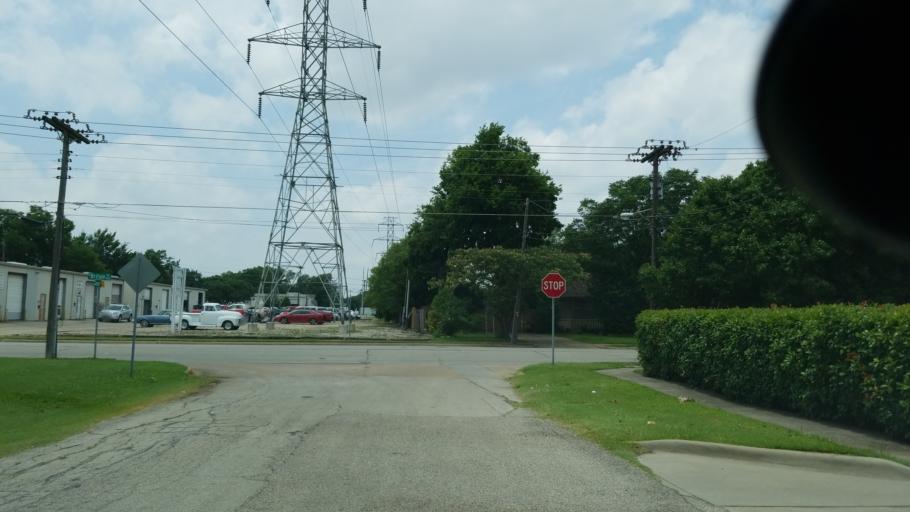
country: US
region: Texas
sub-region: Dallas County
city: Irving
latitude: 32.8170
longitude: -96.9421
